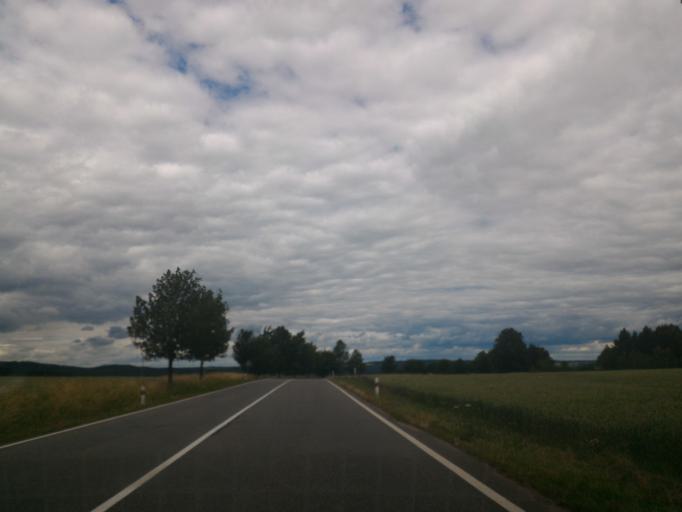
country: CZ
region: Vysocina
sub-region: Okres Pelhrimov
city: Zeliv
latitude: 49.4833
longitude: 15.1801
